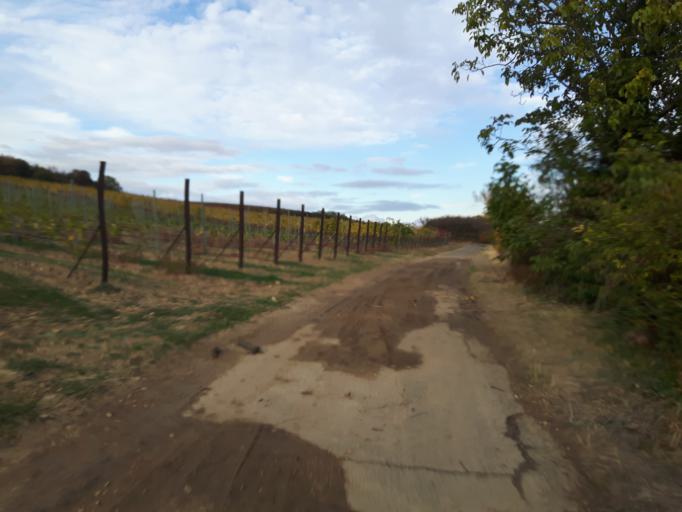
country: DE
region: Rheinland-Pfalz
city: Grunstadt
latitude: 49.5864
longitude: 8.1679
